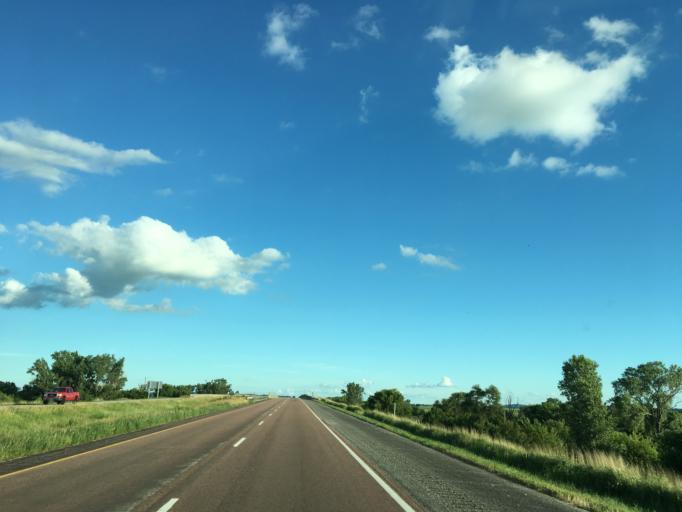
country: US
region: Nebraska
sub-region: Cass County
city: Plattsmouth
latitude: 41.0187
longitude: -95.8123
